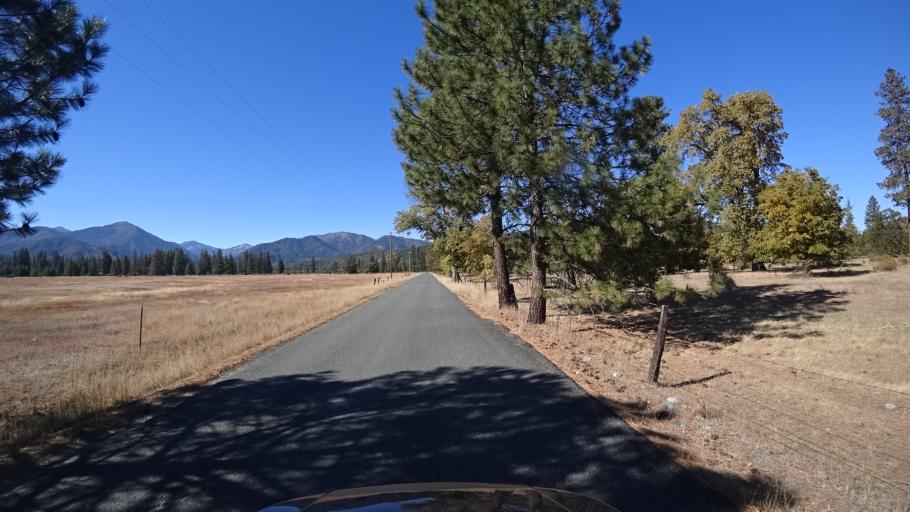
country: US
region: California
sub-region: Siskiyou County
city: Yreka
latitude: 41.5486
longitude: -122.9226
